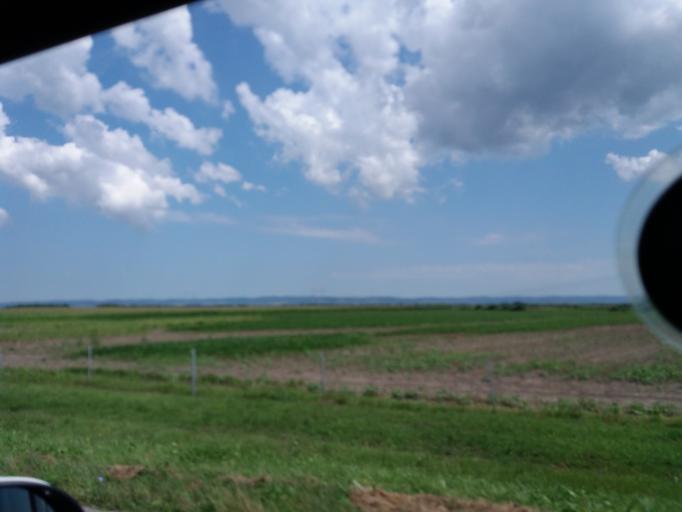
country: RS
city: Sasinci
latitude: 44.9739
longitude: 19.7540
